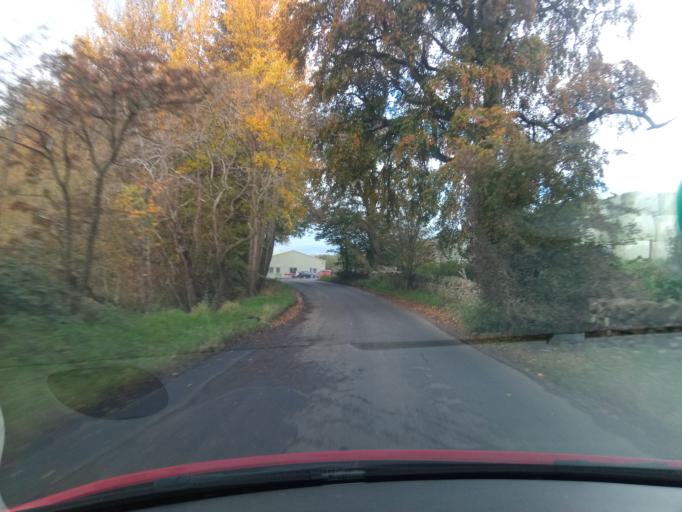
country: GB
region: Scotland
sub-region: The Scottish Borders
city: Peebles
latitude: 55.6444
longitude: -3.1657
